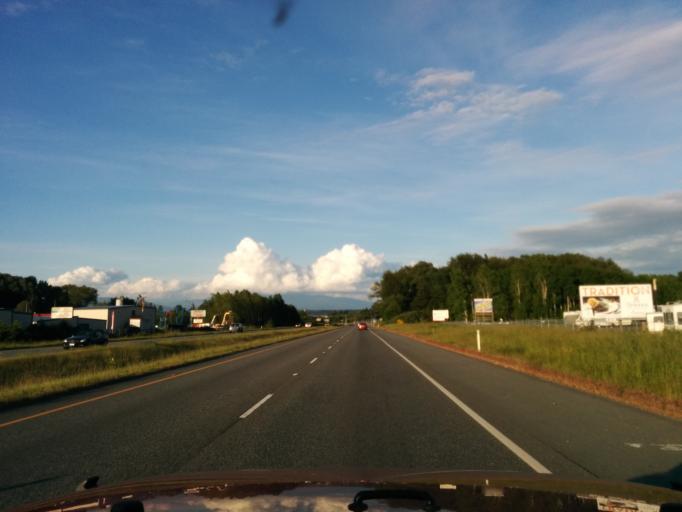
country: US
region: Washington
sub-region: Skagit County
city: Anacortes
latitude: 48.4607
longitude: -122.5543
